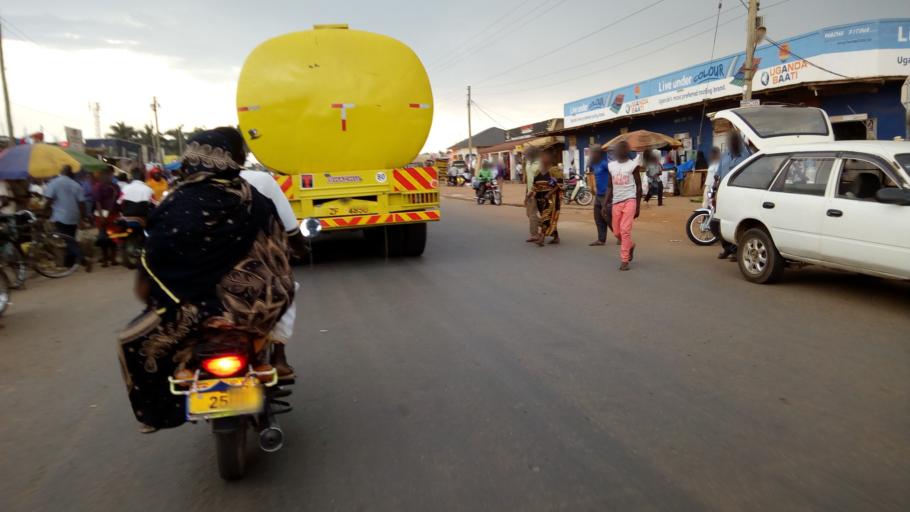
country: UG
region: Eastern Region
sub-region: Mbale District
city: Mbale
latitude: 1.0933
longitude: 34.1765
